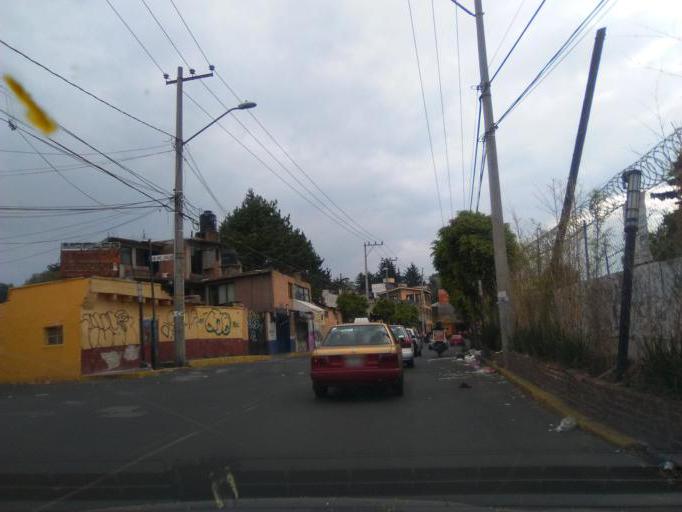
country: MX
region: Mexico City
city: Col. Bosques de las Lomas
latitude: 19.3603
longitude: -99.2523
